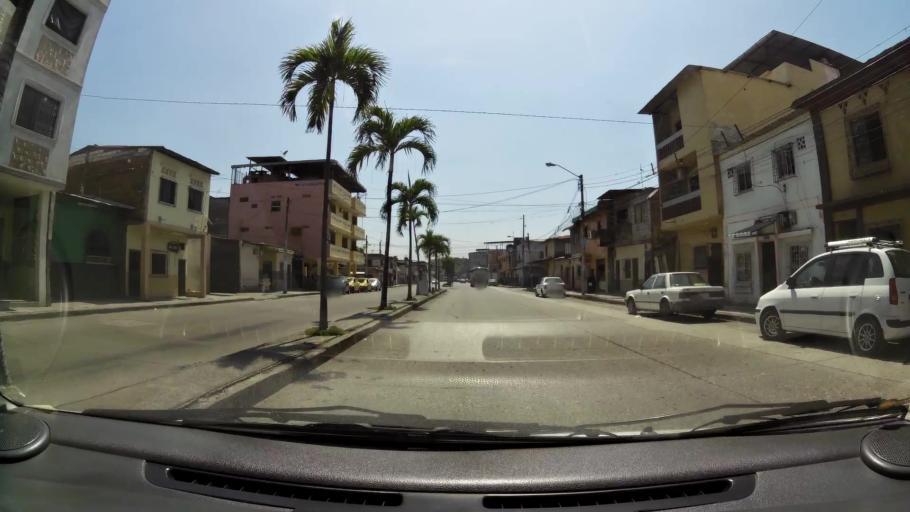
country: EC
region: Guayas
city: Guayaquil
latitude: -2.2006
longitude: -79.9104
